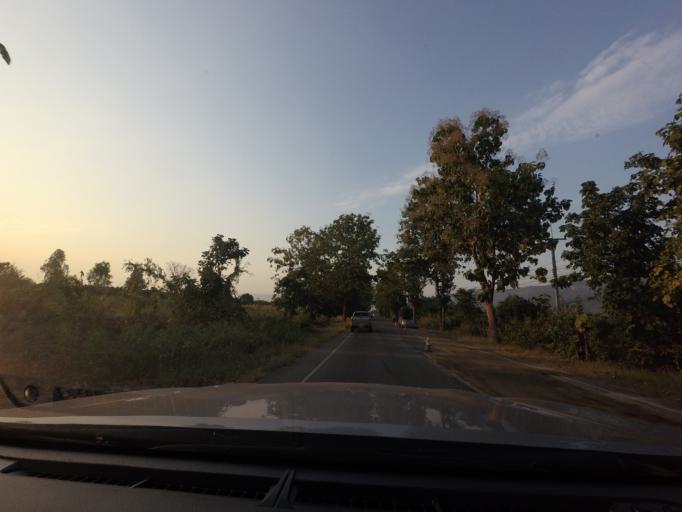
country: TH
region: Phitsanulok
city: Wang Thong
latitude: 16.7005
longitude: 100.5161
